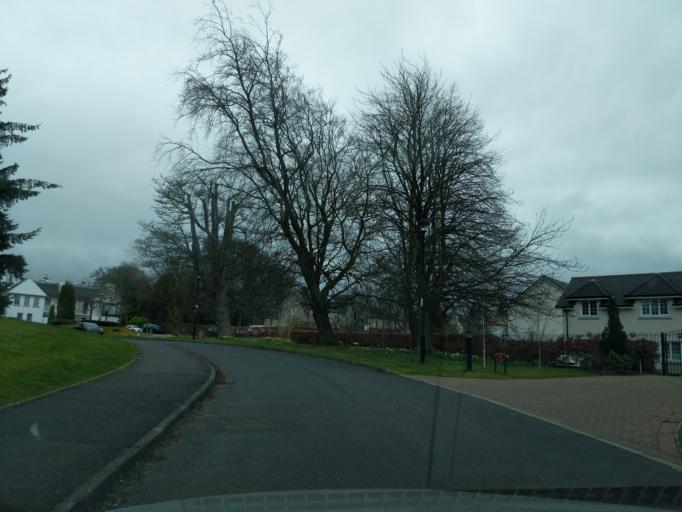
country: GB
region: Scotland
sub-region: Edinburgh
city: Balerno
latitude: 55.8878
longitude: -3.3450
